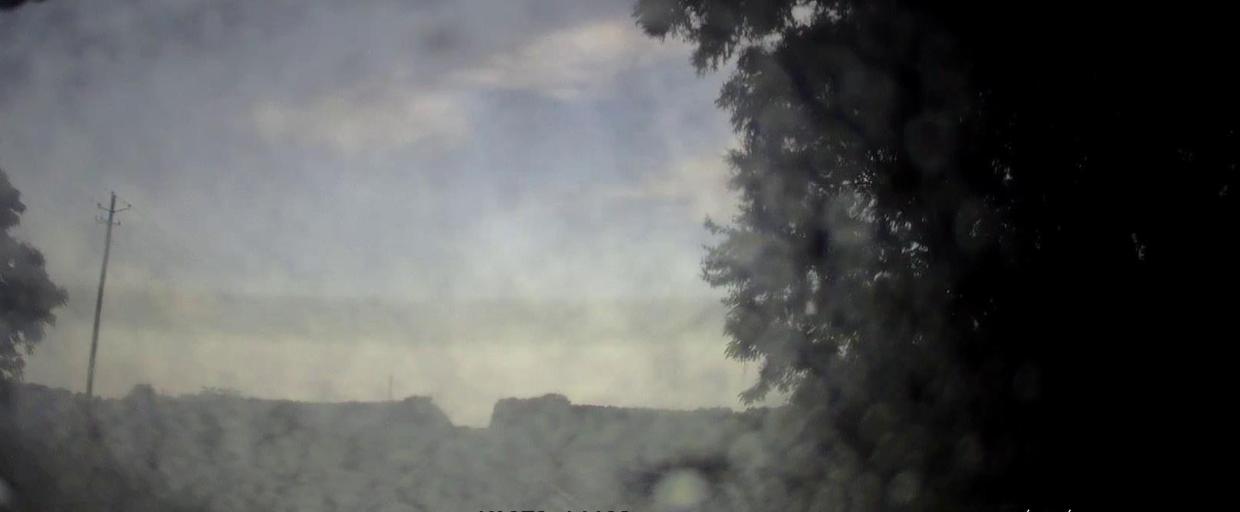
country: US
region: Georgia
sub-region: Dodge County
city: Chester
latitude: 32.5482
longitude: -83.1233
